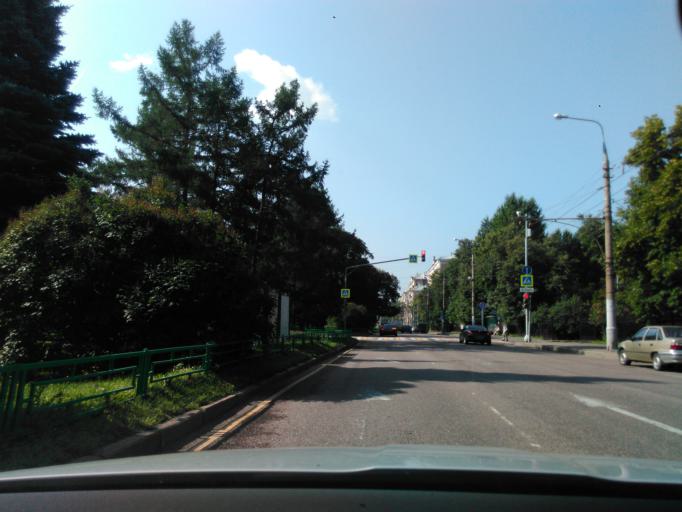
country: RU
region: Moscow
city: Sokol
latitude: 55.7990
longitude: 37.5147
